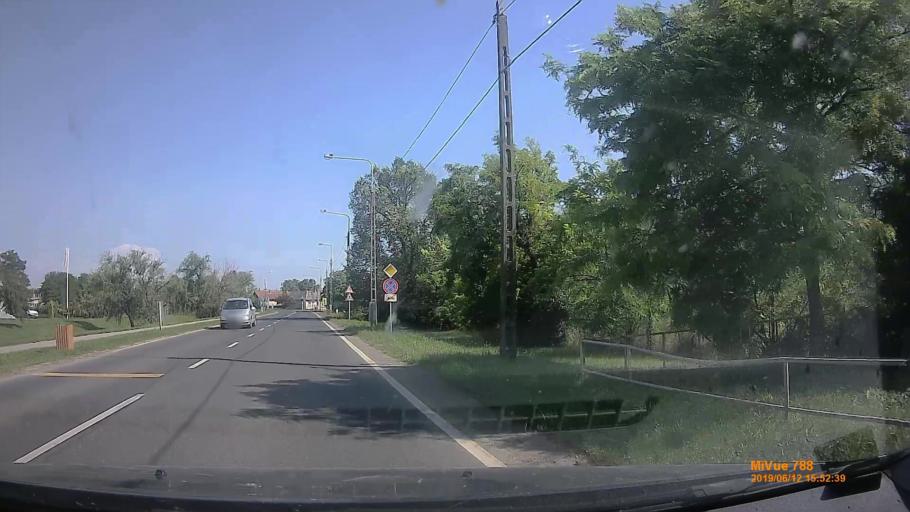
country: HU
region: Csongrad
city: Apatfalva
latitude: 46.1760
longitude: 20.5761
